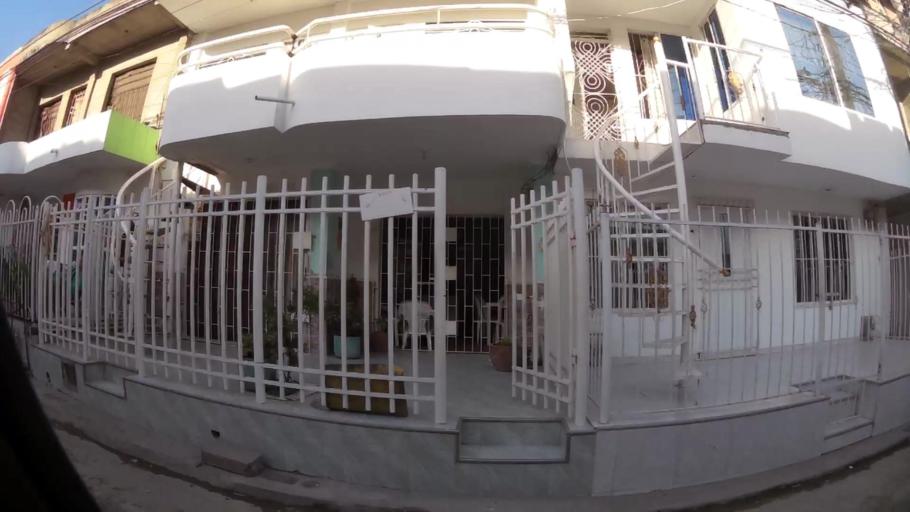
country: CO
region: Bolivar
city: Cartagena
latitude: 10.3987
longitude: -75.4752
